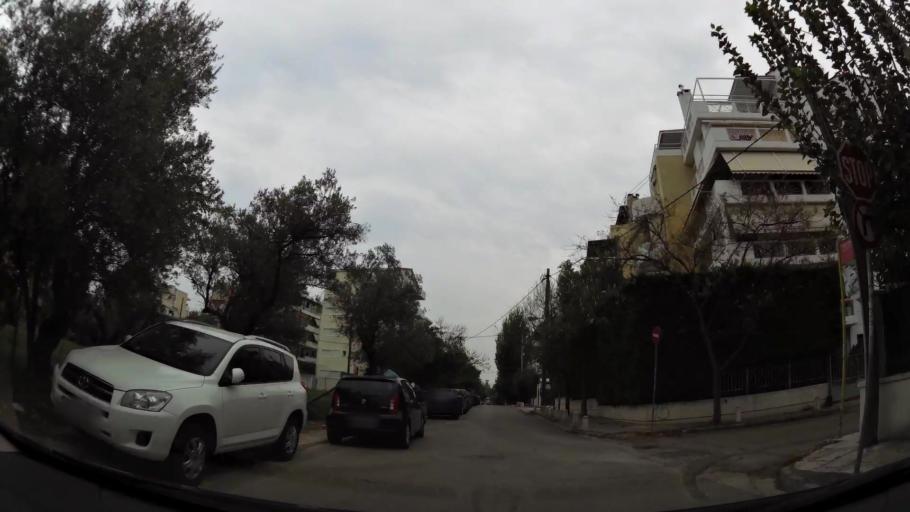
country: GR
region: Attica
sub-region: Nomarchia Athinas
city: Filothei
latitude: 38.0335
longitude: 23.7846
